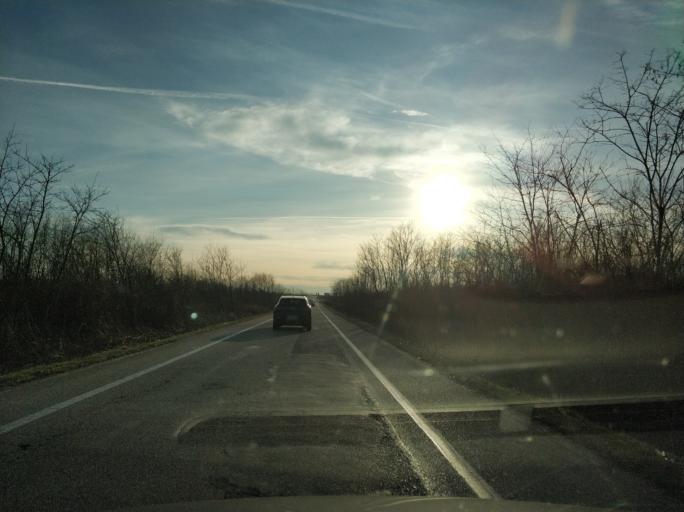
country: IT
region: Piedmont
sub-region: Provincia di Torino
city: Volpiano
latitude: 45.1892
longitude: 7.7822
